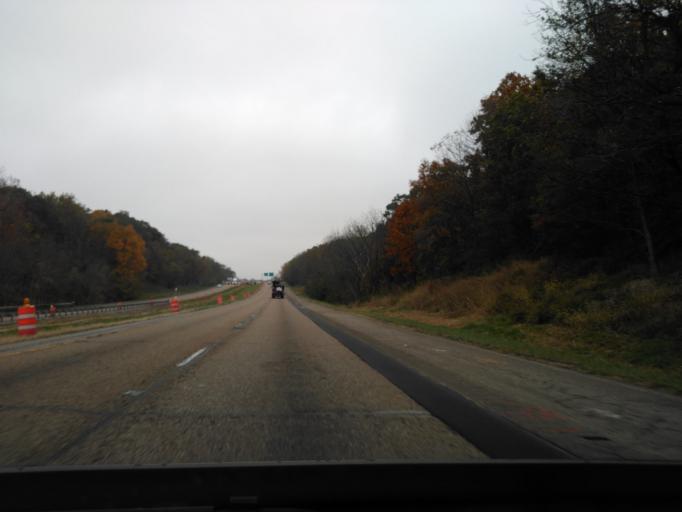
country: US
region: Illinois
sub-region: Madison County
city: Troy
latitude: 38.7553
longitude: -89.8808
